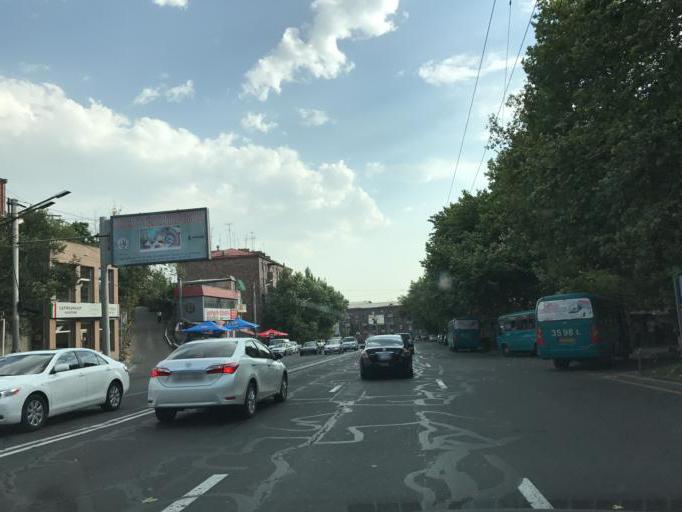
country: AM
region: Yerevan
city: Yerevan
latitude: 40.1885
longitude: 44.5274
